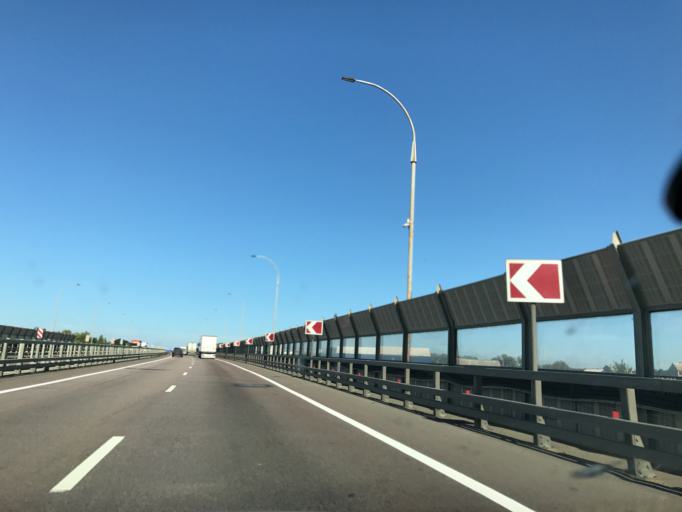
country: RU
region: Voronezj
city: Verkhniy Mamon
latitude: 50.1756
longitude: 40.4272
